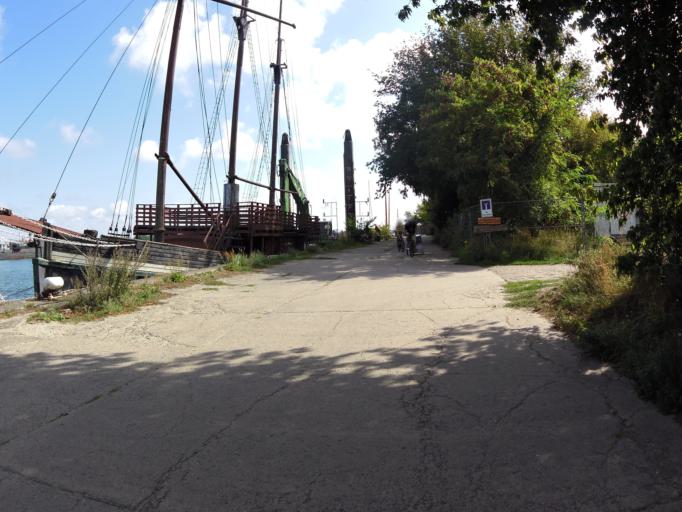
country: DE
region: Mecklenburg-Vorpommern
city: Kroslin
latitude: 54.1354
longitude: 13.7631
